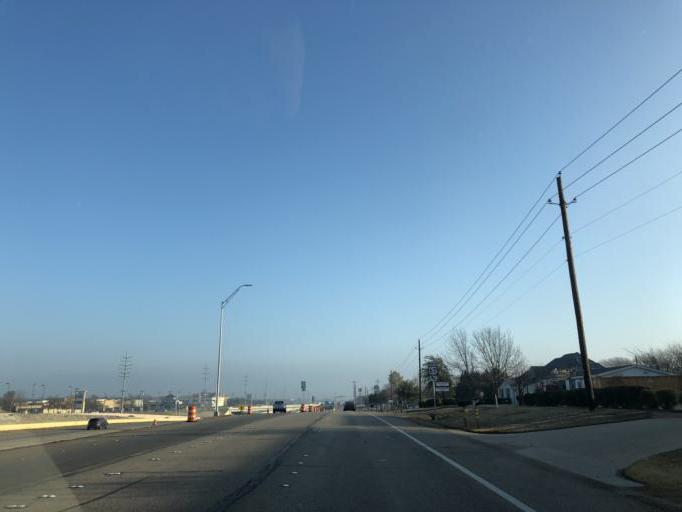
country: US
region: Texas
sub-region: Dallas County
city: Cedar Hill
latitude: 32.6011
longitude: -96.9340
